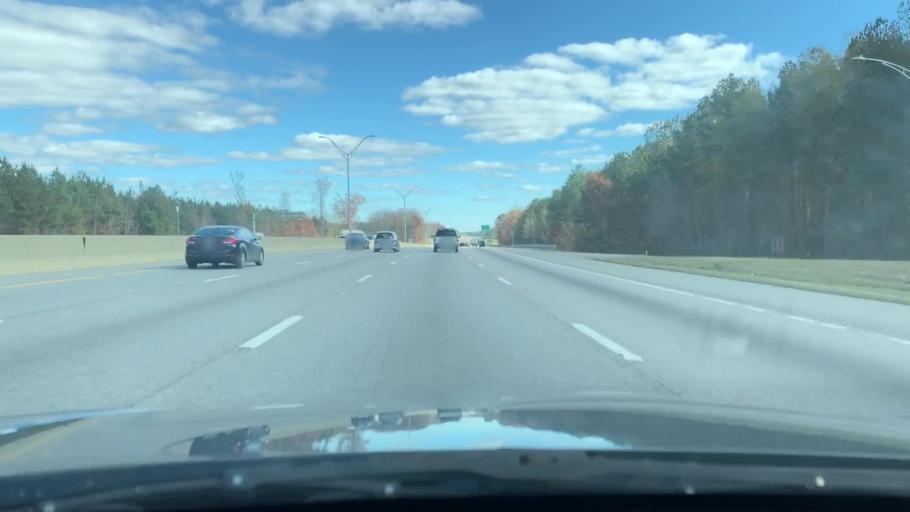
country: US
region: North Carolina
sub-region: Alamance County
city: Mebane
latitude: 36.0792
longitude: -79.2218
